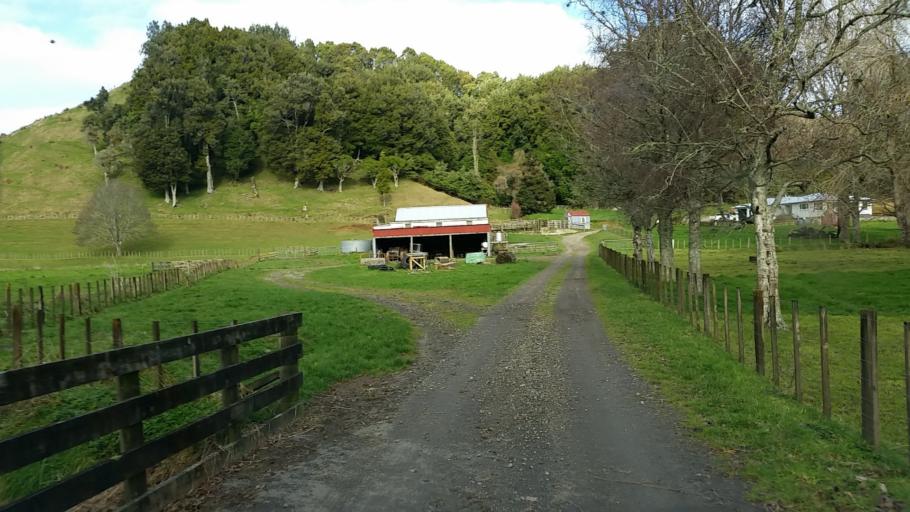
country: NZ
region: Taranaki
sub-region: South Taranaki District
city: Eltham
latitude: -39.2511
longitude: 174.5428
